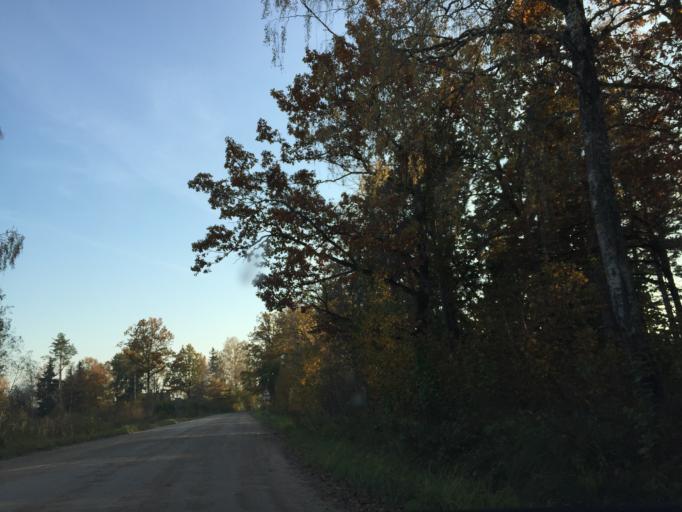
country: LV
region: Vainode
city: Vainode
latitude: 56.6214
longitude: 21.8173
